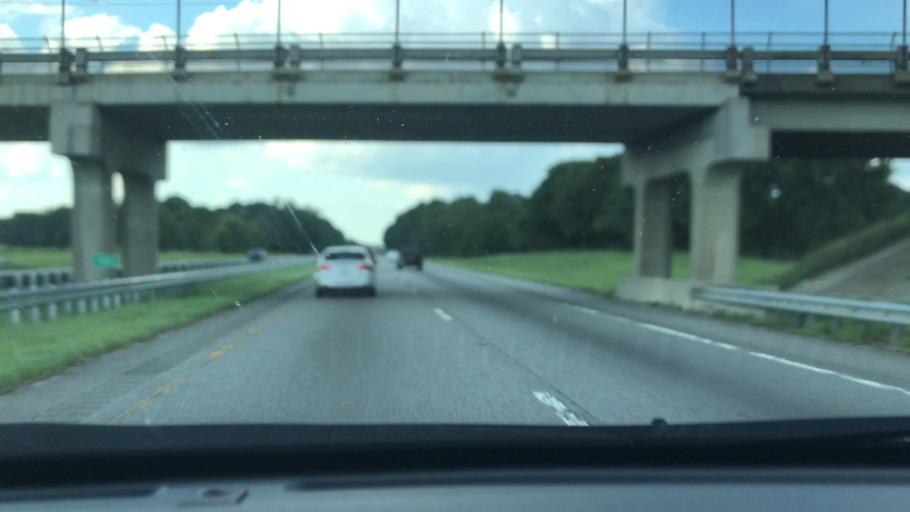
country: US
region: North Carolina
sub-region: Robeson County
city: Saint Pauls
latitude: 34.8805
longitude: -78.9617
